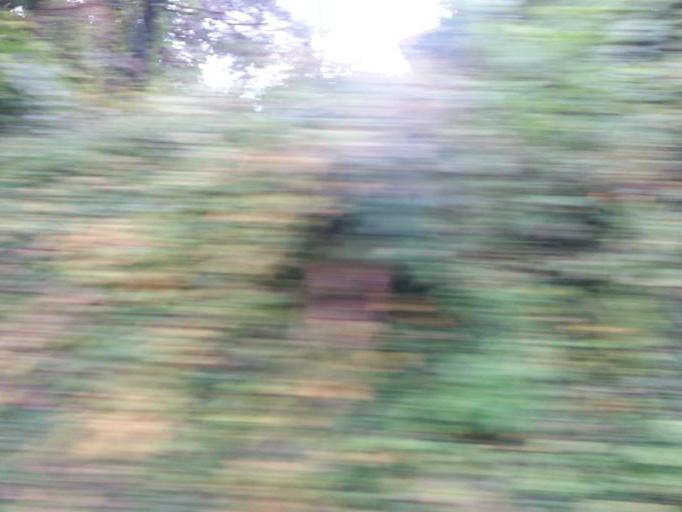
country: US
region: Tennessee
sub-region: Knox County
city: Mascot
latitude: 36.1176
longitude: -83.7756
